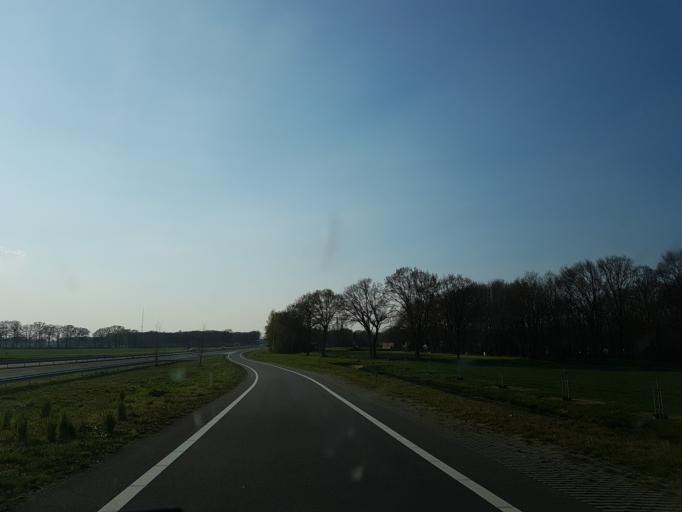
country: NL
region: Overijssel
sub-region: Gemeente Raalte
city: Heino
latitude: 52.4840
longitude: 6.1769
